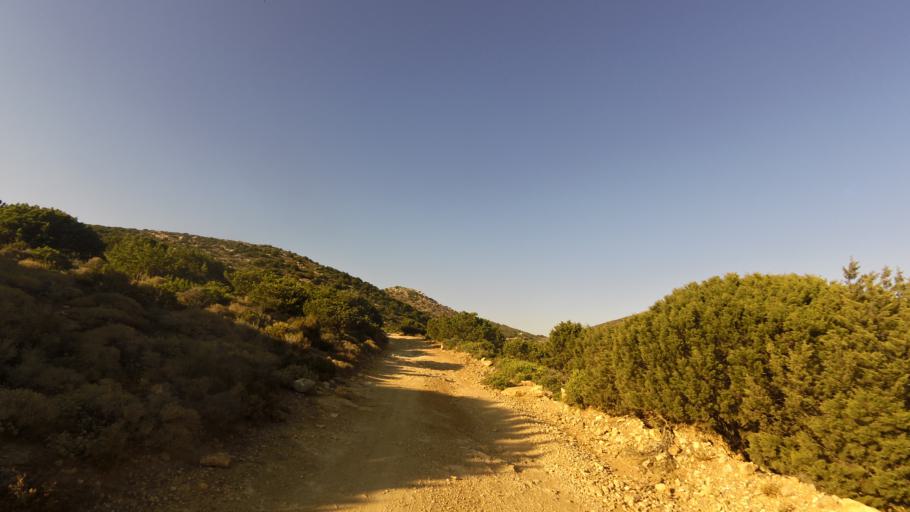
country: GR
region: South Aegean
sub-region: Nomos Kykladon
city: Antiparos
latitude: 36.9926
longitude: 25.0312
